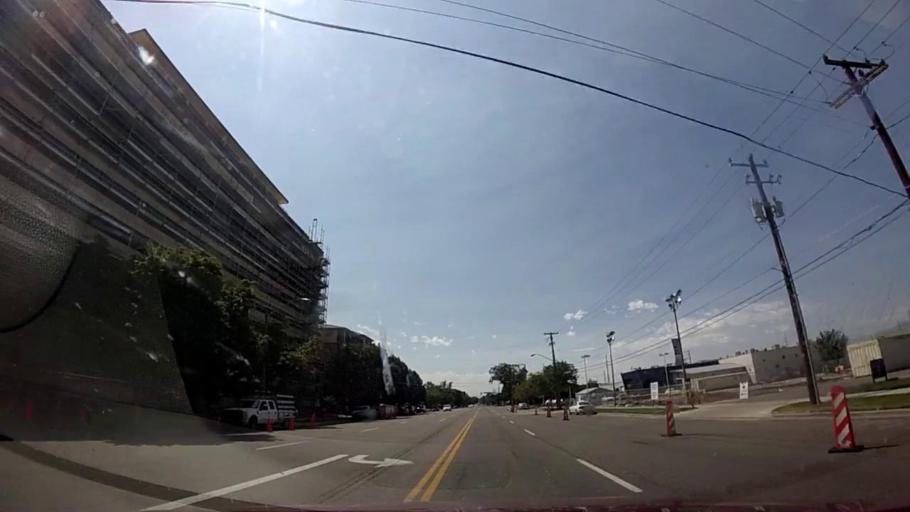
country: US
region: Utah
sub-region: Salt Lake County
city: Salt Lake City
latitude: 40.7578
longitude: -111.8854
